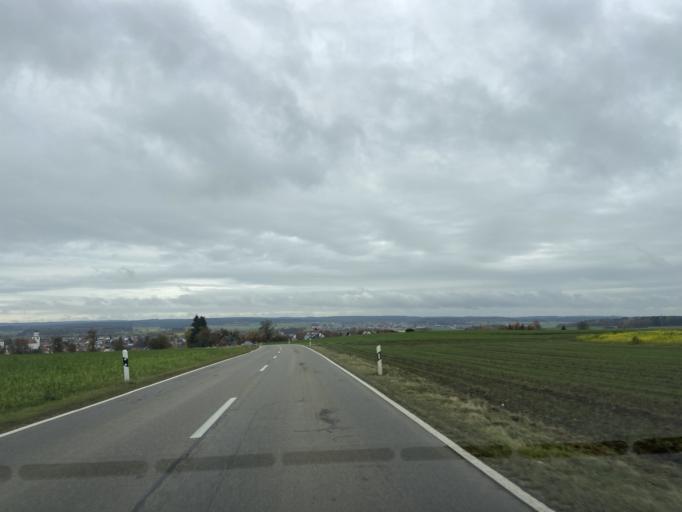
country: DE
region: Baden-Wuerttemberg
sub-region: Tuebingen Region
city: Messkirch
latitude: 47.9891
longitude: 9.1260
